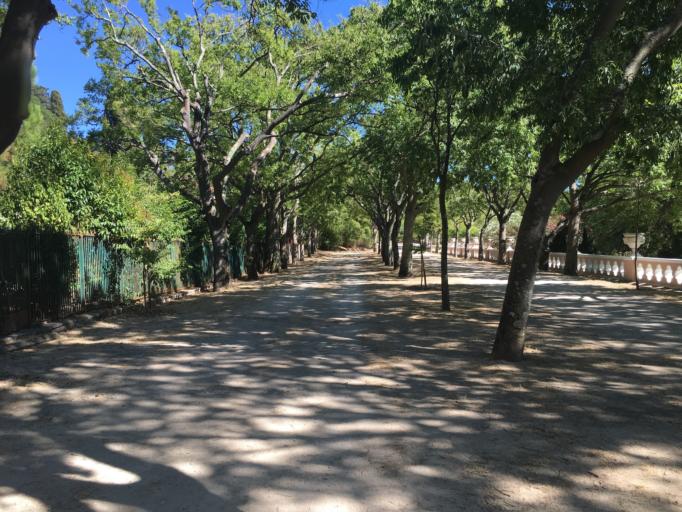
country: PT
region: Setubal
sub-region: Almada
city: Cacilhas
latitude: 38.7094
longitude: -9.1701
